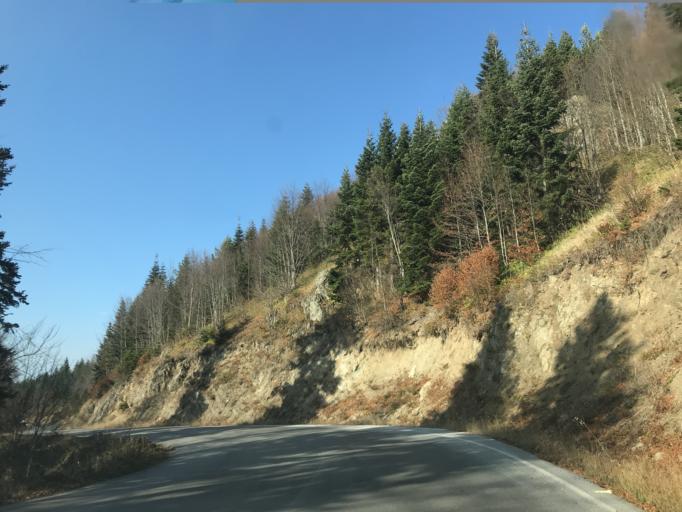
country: TR
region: Bolu
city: Bolu
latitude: 40.8871
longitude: 31.6805
